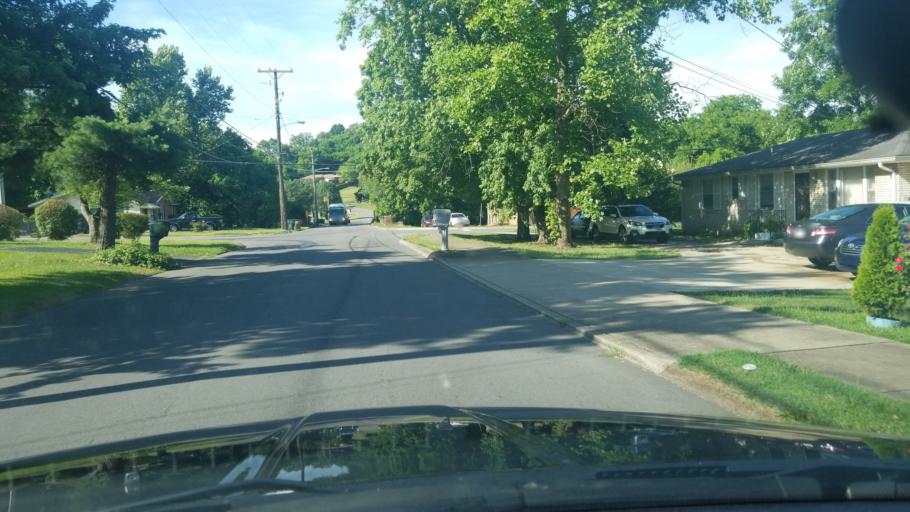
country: US
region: Tennessee
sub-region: Davidson County
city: Nashville
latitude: 36.2319
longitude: -86.7734
